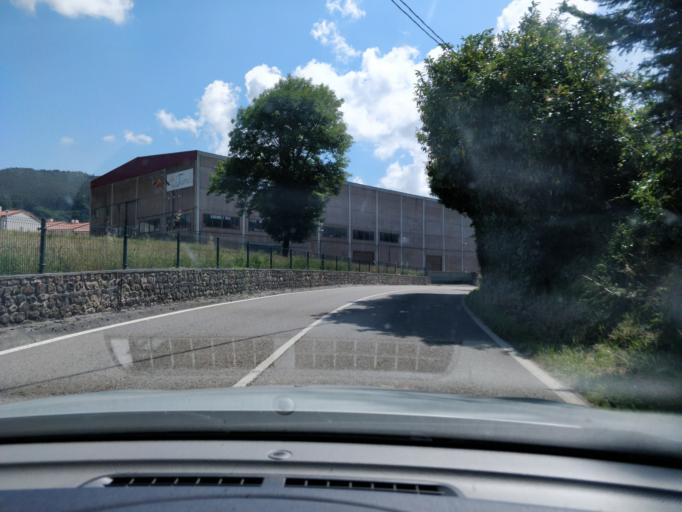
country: ES
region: Cantabria
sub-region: Provincia de Cantabria
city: Corvera
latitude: 43.2709
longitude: -3.9310
